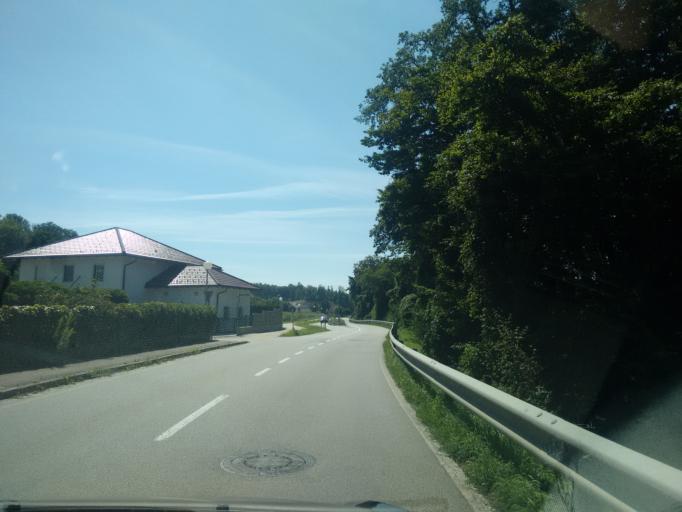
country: DE
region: Bavaria
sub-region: Lower Bavaria
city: Kirchdorf am Inn
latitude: 48.2302
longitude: 13.0082
